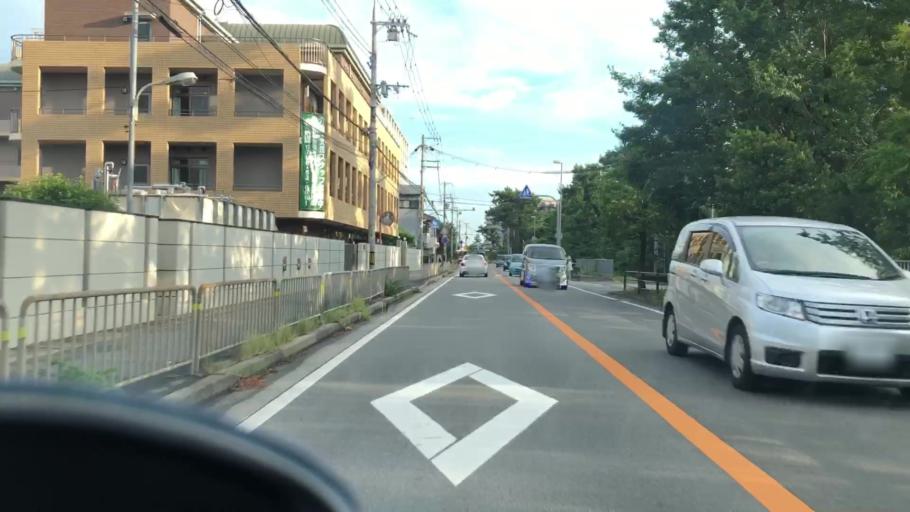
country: JP
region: Hyogo
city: Takarazuka
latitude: 34.7778
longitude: 135.3713
